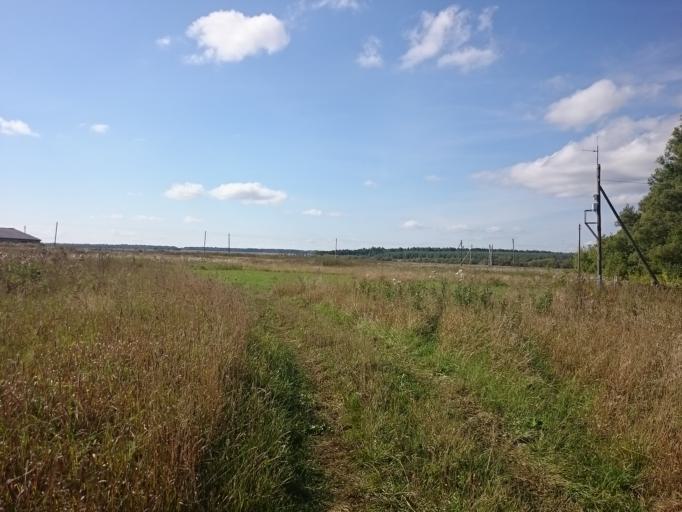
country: RU
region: Mordoviya
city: Kadoshkino
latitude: 54.0321
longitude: 44.4910
